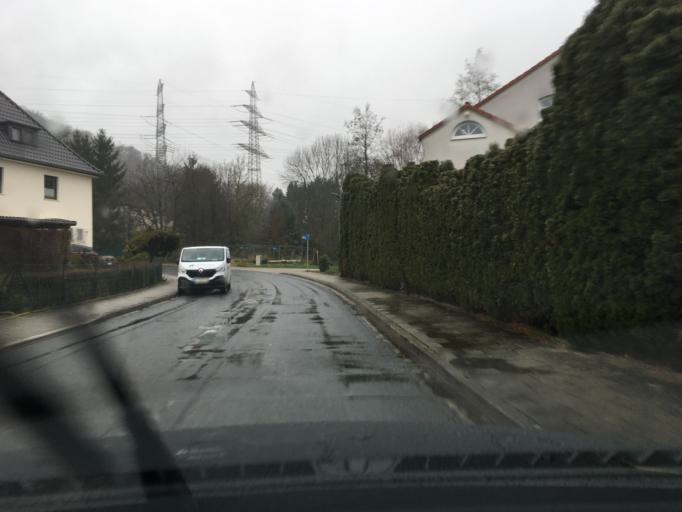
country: DE
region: North Rhine-Westphalia
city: Hattingen
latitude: 51.3862
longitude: 7.1710
